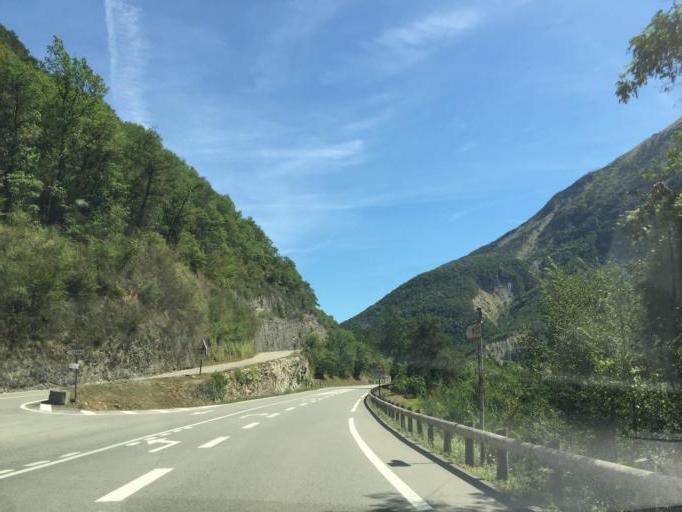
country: FR
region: Provence-Alpes-Cote d'Azur
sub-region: Departement des Alpes-Maritimes
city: Gilette
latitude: 43.9822
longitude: 7.1392
